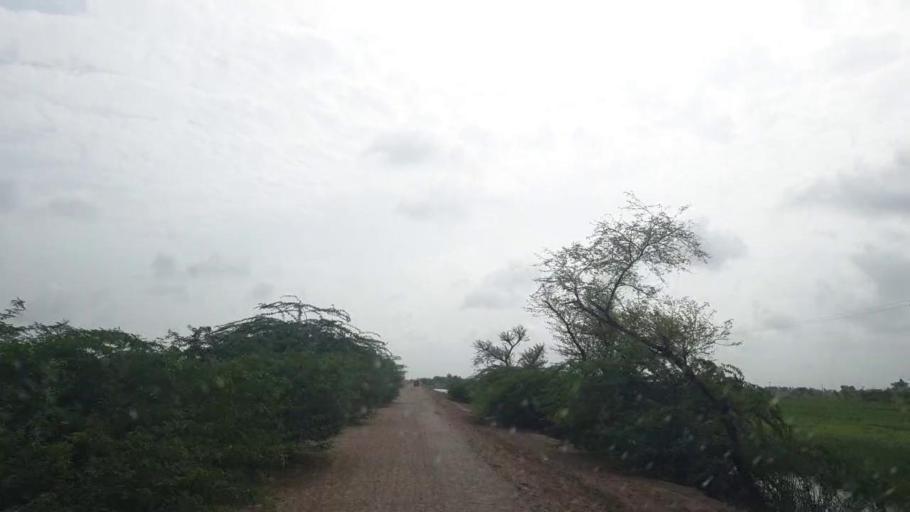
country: PK
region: Sindh
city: Tando Bago
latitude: 24.8030
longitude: 69.0104
